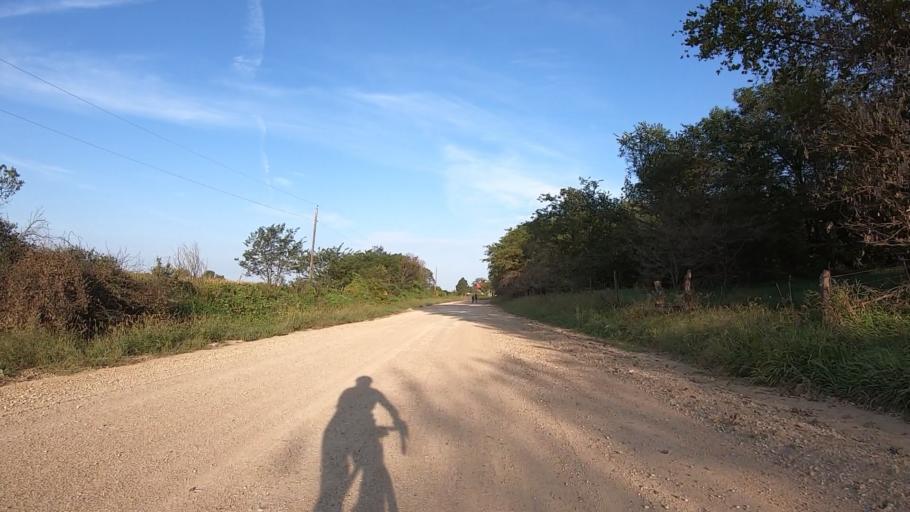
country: US
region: Kansas
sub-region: Marshall County
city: Blue Rapids
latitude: 39.7222
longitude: -96.7765
